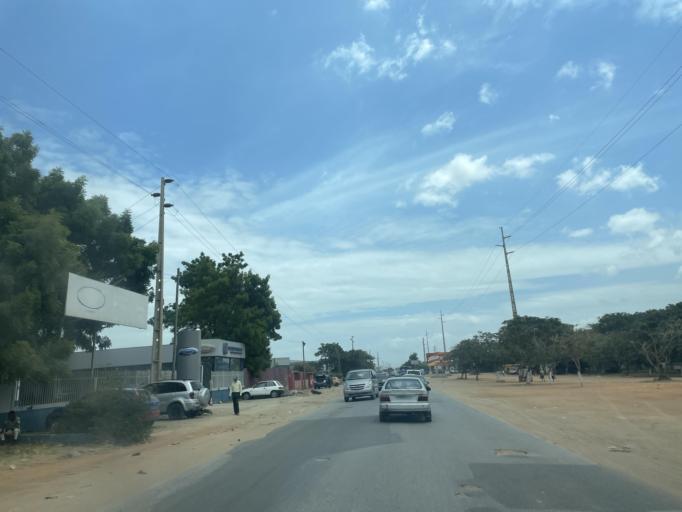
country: AO
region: Luanda
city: Luanda
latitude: -8.9431
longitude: 13.3841
